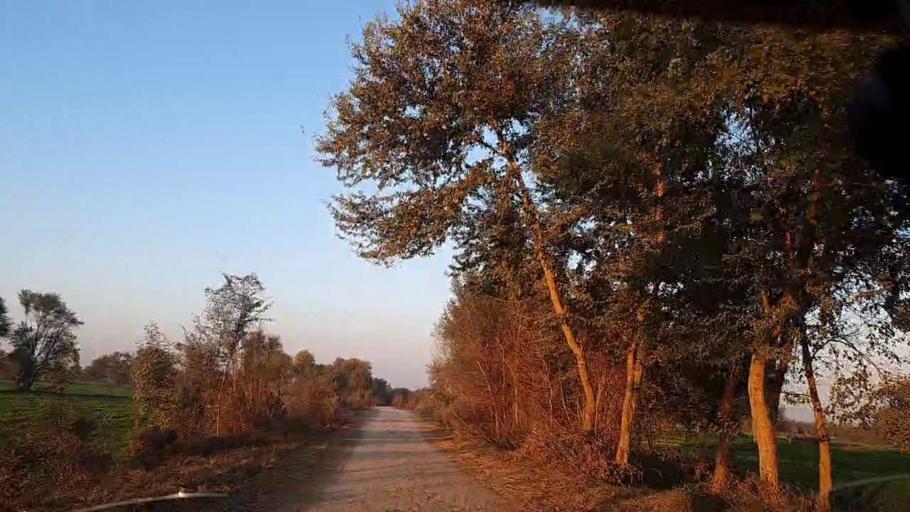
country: PK
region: Sindh
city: Adilpur
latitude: 27.8341
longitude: 69.2969
